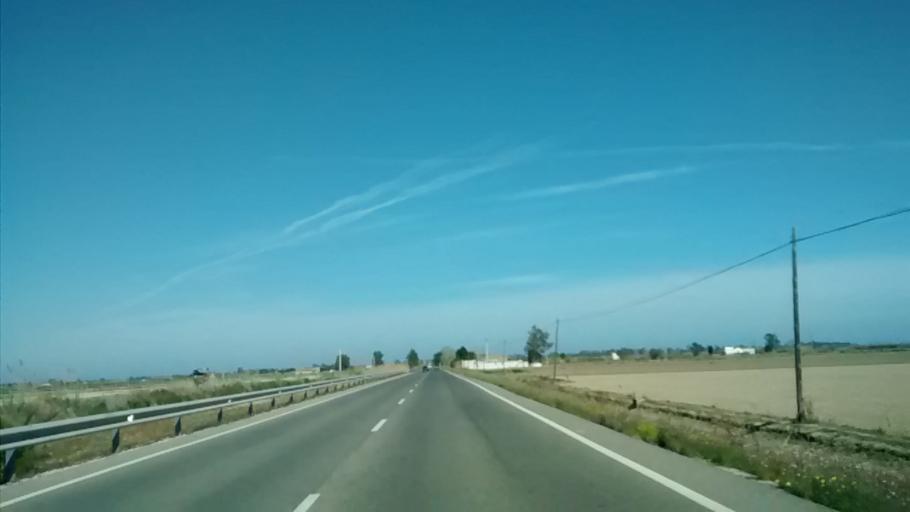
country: ES
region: Catalonia
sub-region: Provincia de Tarragona
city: Deltebre
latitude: 40.7053
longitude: 0.7990
